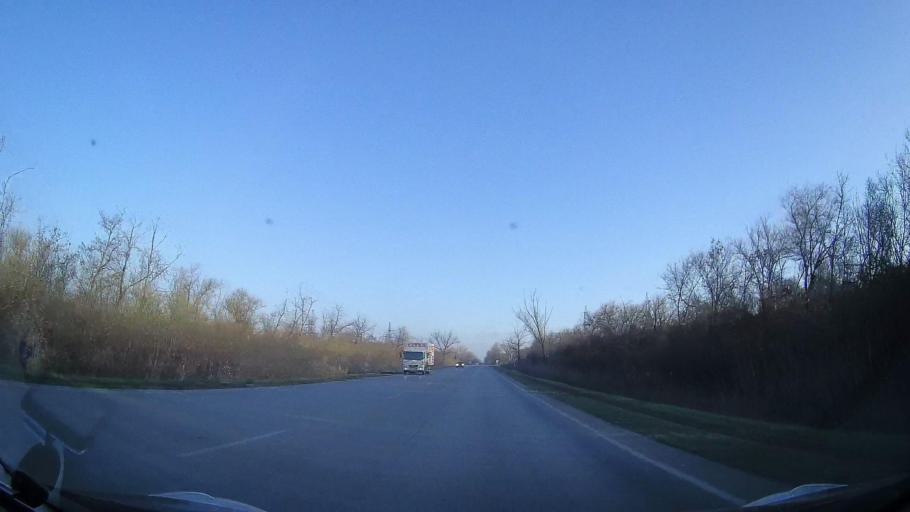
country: RU
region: Rostov
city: Bataysk
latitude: 47.0518
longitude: 39.8348
